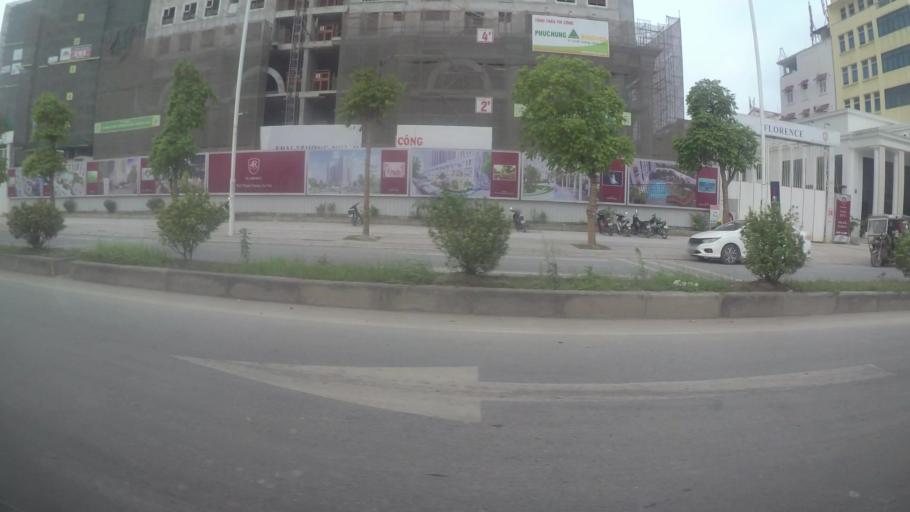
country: VN
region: Ha Noi
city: Cau Dien
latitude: 21.0302
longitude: 105.7612
